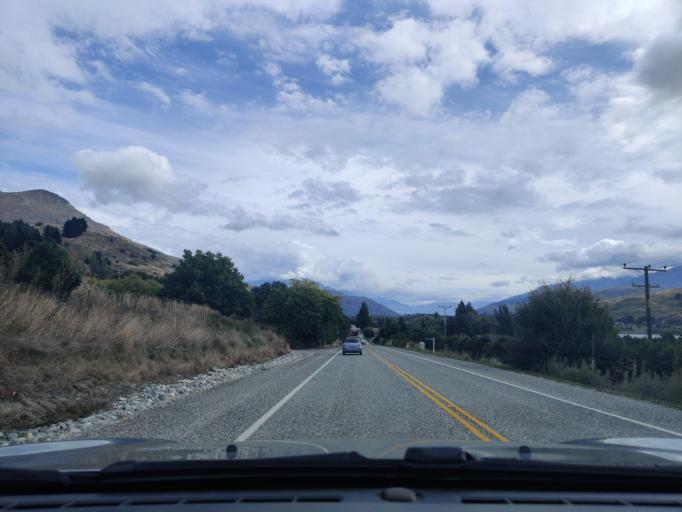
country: NZ
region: Otago
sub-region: Queenstown-Lakes District
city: Arrowtown
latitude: -44.9860
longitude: 168.8181
